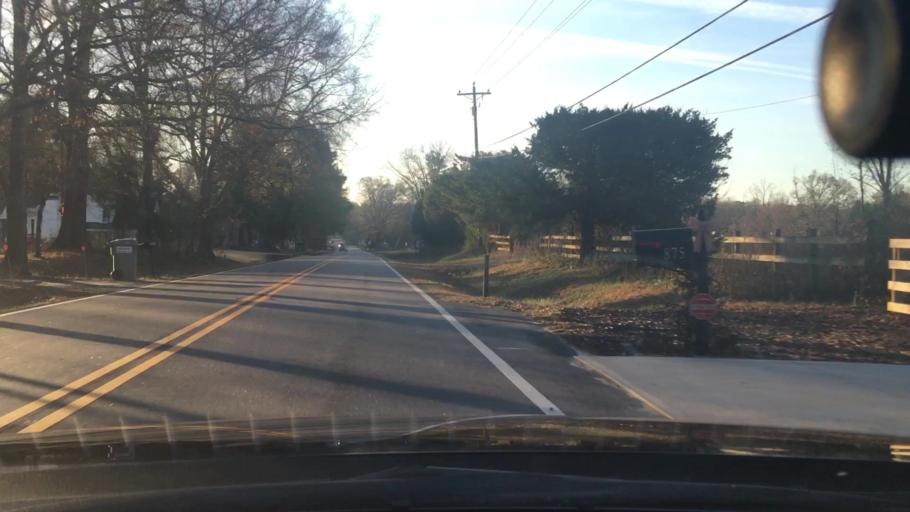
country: US
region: Georgia
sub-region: Coweta County
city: Senoia
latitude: 33.2955
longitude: -84.4606
